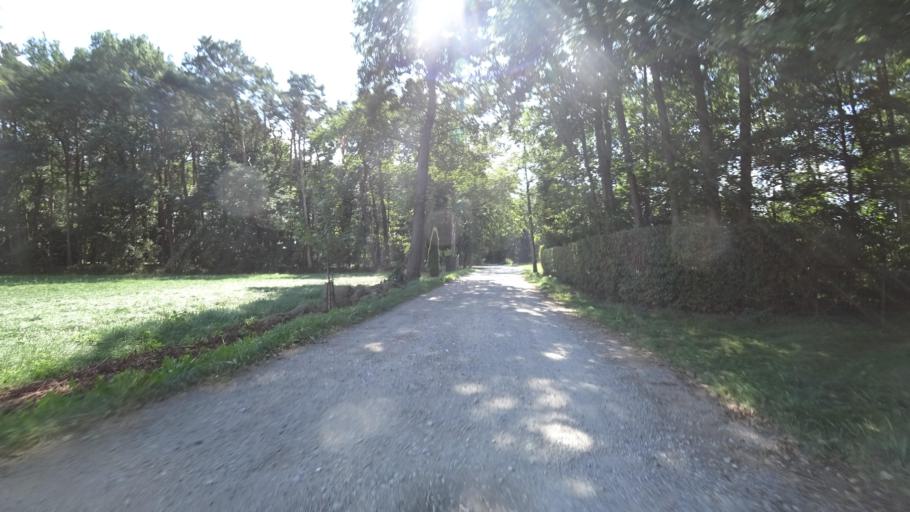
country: DE
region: North Rhine-Westphalia
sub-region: Regierungsbezirk Detmold
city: Guetersloh
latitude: 51.9344
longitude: 8.3983
